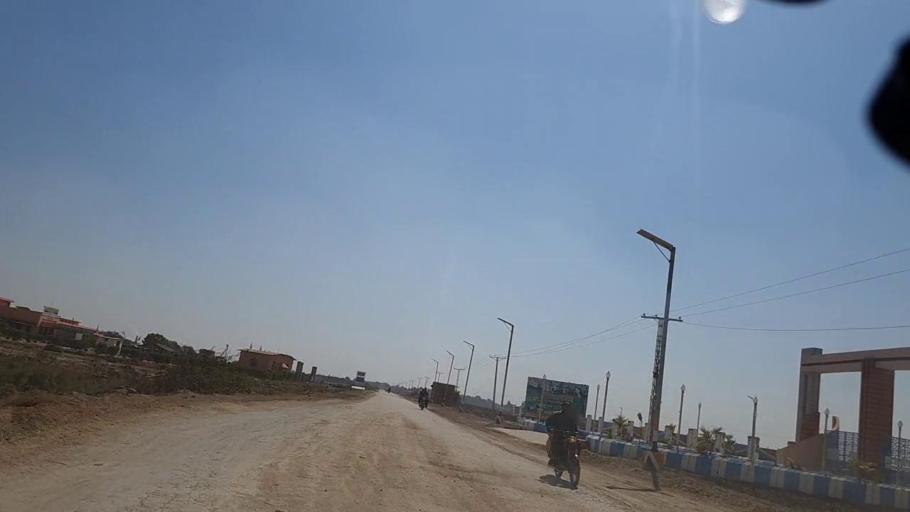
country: PK
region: Sindh
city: Mirpur Khas
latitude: 25.4960
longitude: 69.0372
